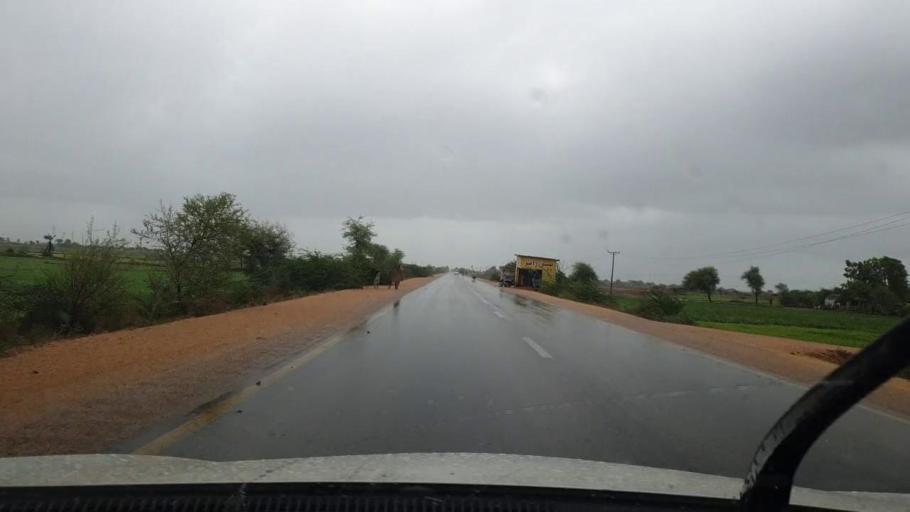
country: PK
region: Sindh
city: Kario
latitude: 24.6532
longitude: 68.5886
